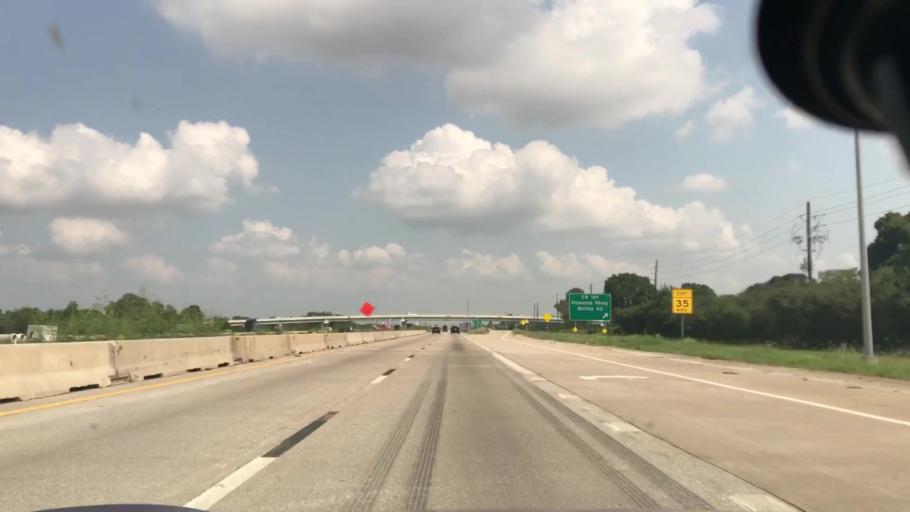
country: US
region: Texas
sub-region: Brazoria County
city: Iowa Colony
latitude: 29.5217
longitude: -95.3865
